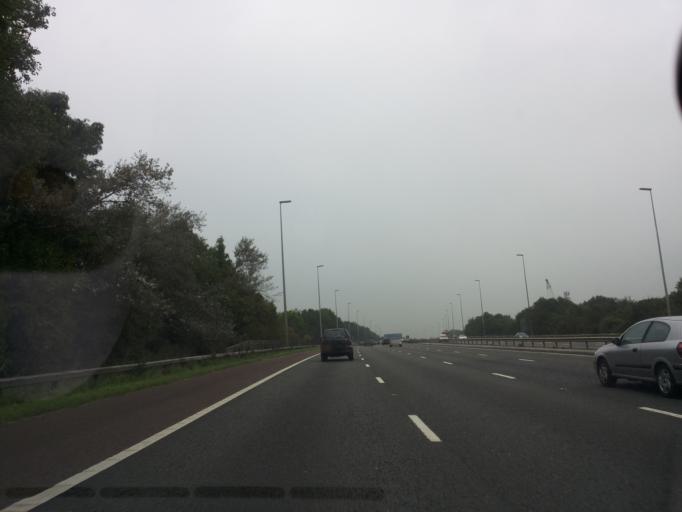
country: GB
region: England
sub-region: Lancashire
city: Goosnargh
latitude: 53.7785
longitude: -2.6470
